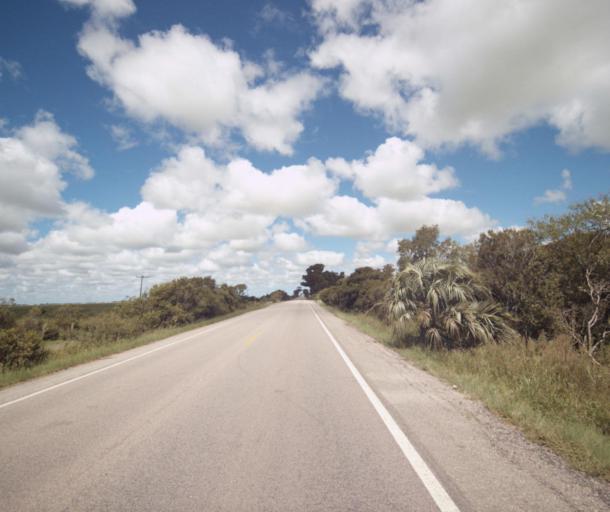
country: BR
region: Rio Grande do Sul
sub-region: Rio Grande
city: Rio Grande
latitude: -32.1832
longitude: -52.4258
